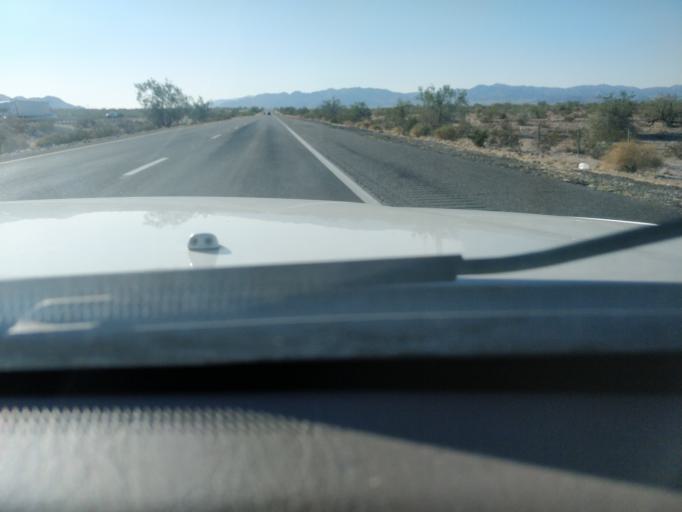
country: US
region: California
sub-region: Imperial County
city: Niland
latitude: 33.7033
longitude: -115.3207
